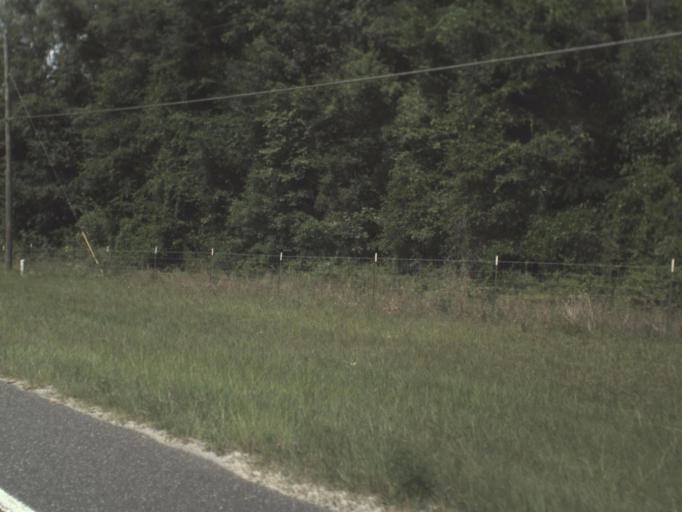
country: US
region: Florida
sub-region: Columbia County
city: Lake City
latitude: 30.0598
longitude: -82.7006
